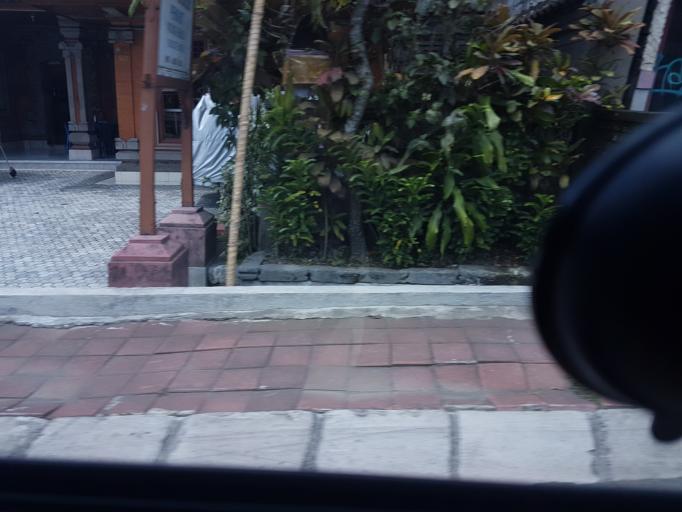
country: ID
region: Bali
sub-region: Kabupaten Gianyar
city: Ubud
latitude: -8.5343
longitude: 115.2724
